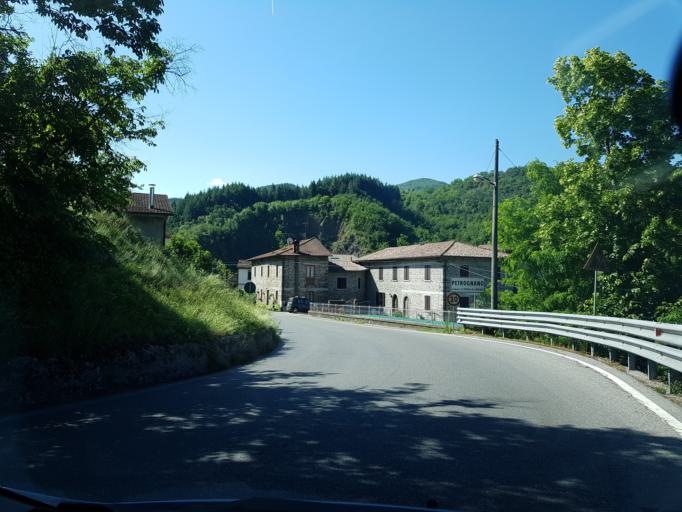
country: IT
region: Tuscany
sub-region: Provincia di Lucca
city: Piazza al Serchio-San Michele
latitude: 44.1755
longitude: 10.3123
